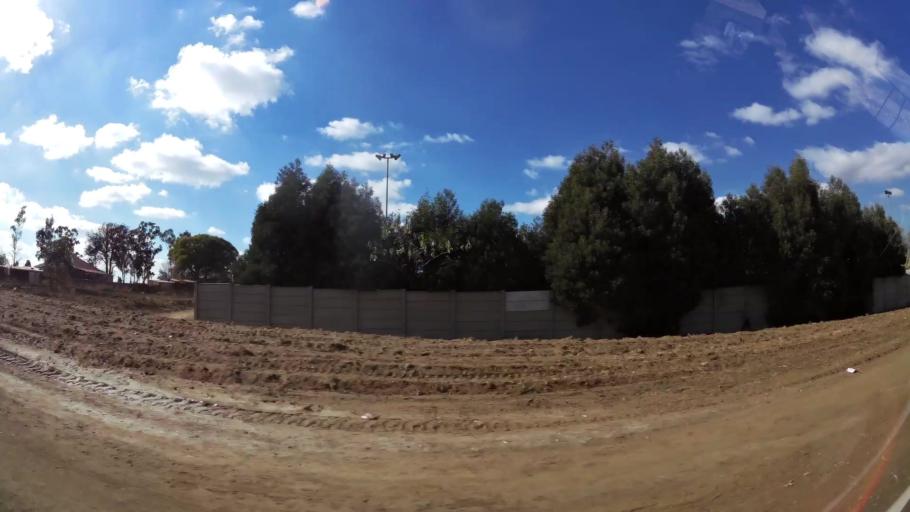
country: ZA
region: Gauteng
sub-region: West Rand District Municipality
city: Krugersdorp
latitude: -26.1270
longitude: 27.8024
